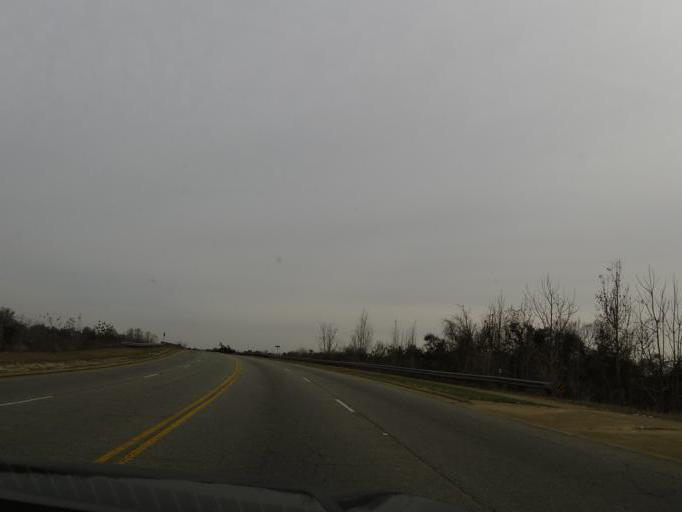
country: US
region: Georgia
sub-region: Decatur County
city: Bainbridge
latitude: 30.9110
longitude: -84.5830
